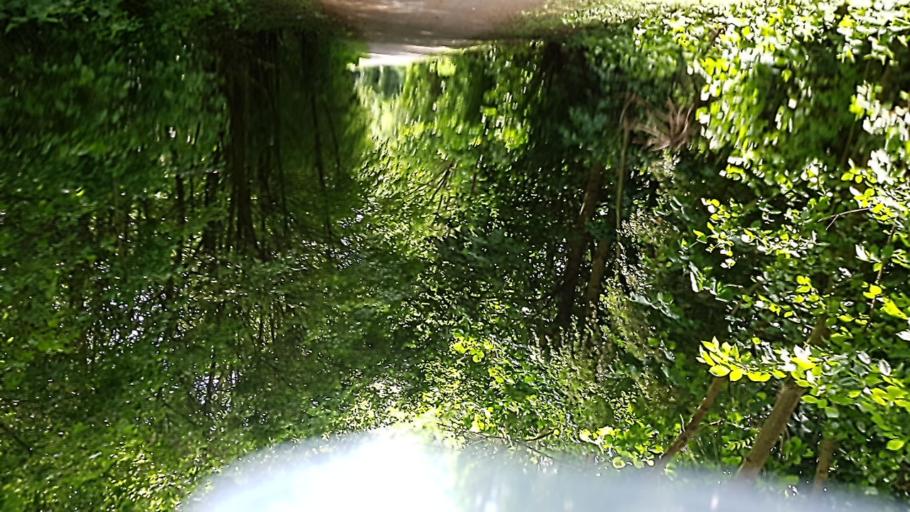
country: FR
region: Nord-Pas-de-Calais
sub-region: Departement du Nord
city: Conde-sur-l'Escaut
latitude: 50.4445
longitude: 3.5866
